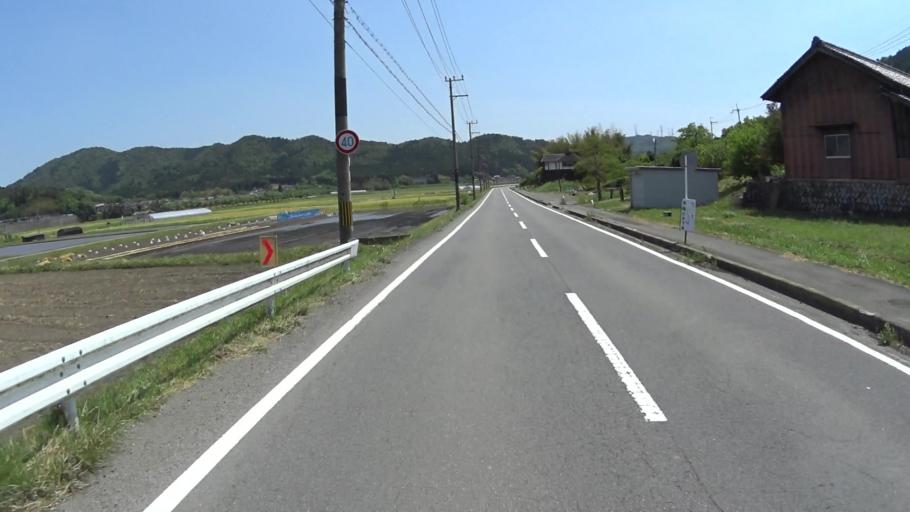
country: JP
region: Kyoto
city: Kameoka
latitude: 35.0241
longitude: 135.4877
